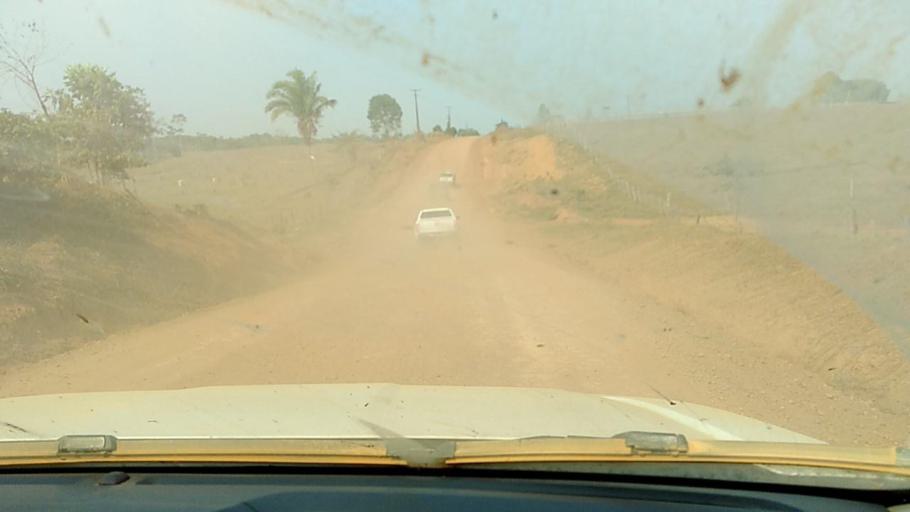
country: BR
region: Rondonia
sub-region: Porto Velho
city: Porto Velho
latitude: -8.8479
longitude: -64.1654
